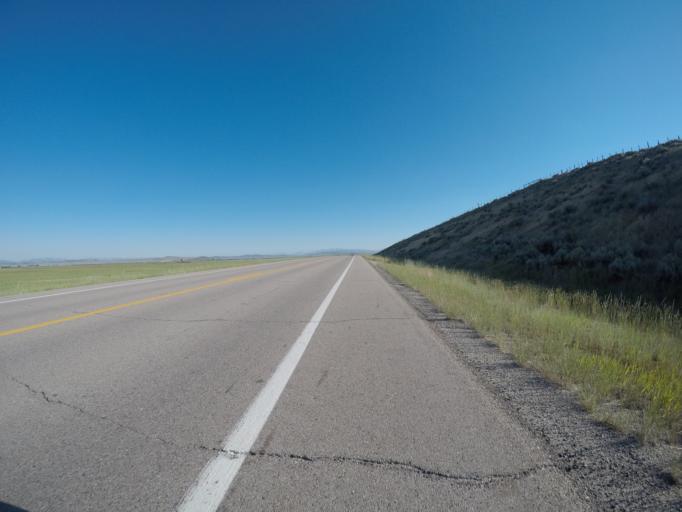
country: US
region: Wyoming
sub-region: Sublette County
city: Pinedale
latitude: 42.9439
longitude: -110.0838
